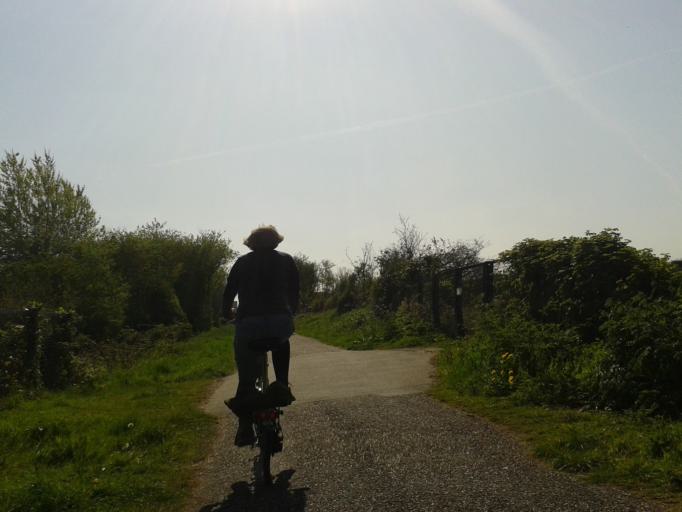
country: GB
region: England
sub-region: Devon
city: Braunton
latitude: 51.0979
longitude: -4.1580
